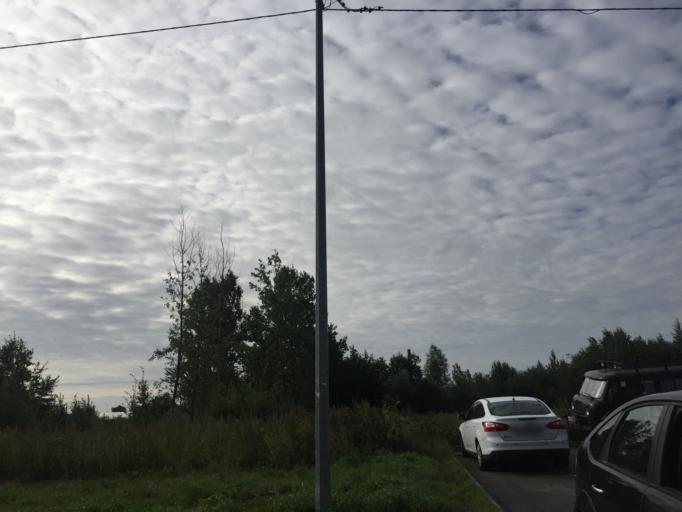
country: RU
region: St.-Petersburg
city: Shushary
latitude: 59.8289
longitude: 30.3707
